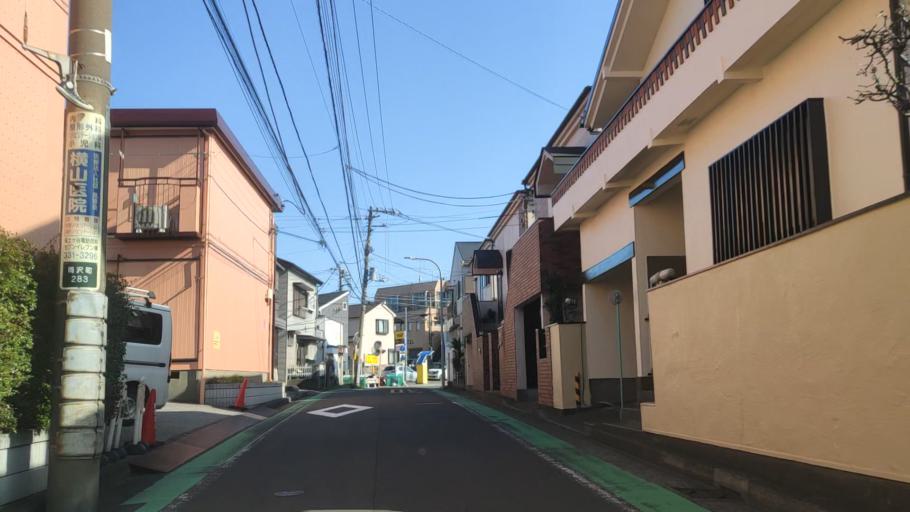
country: JP
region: Kanagawa
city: Yokohama
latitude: 35.4654
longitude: 139.5983
